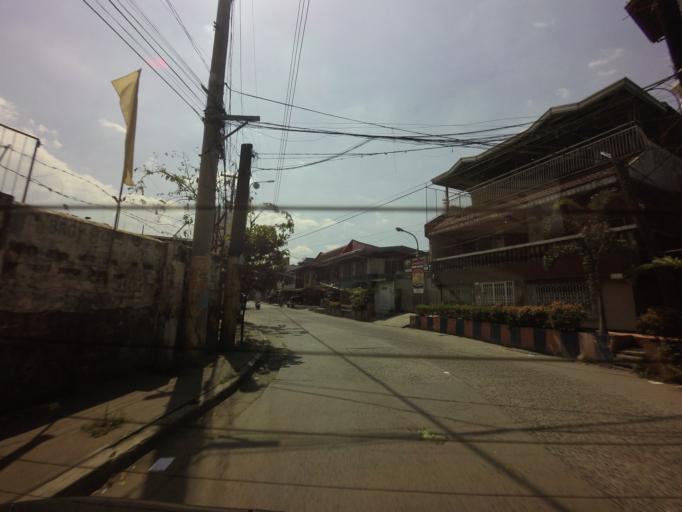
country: PH
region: Metro Manila
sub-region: City of Manila
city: Manila
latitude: 14.6245
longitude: 120.9644
